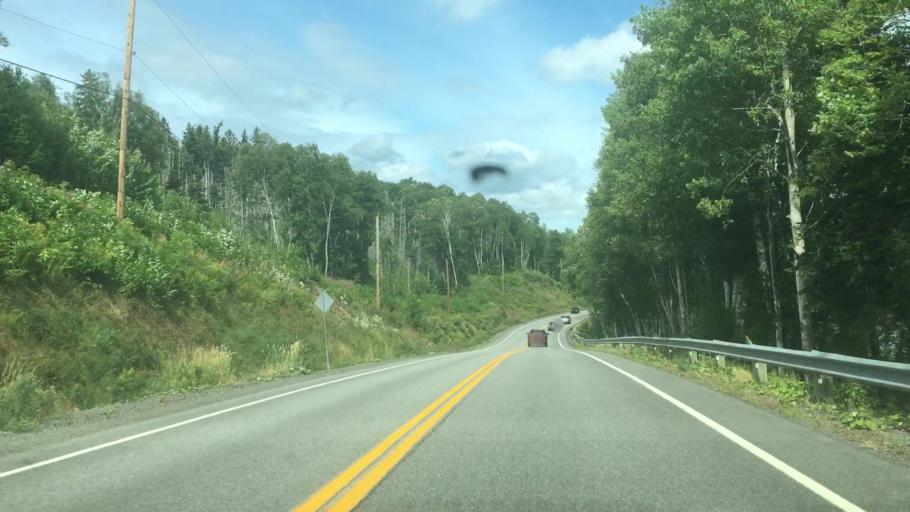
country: CA
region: Nova Scotia
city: Sydney Mines
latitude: 46.2688
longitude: -60.6088
